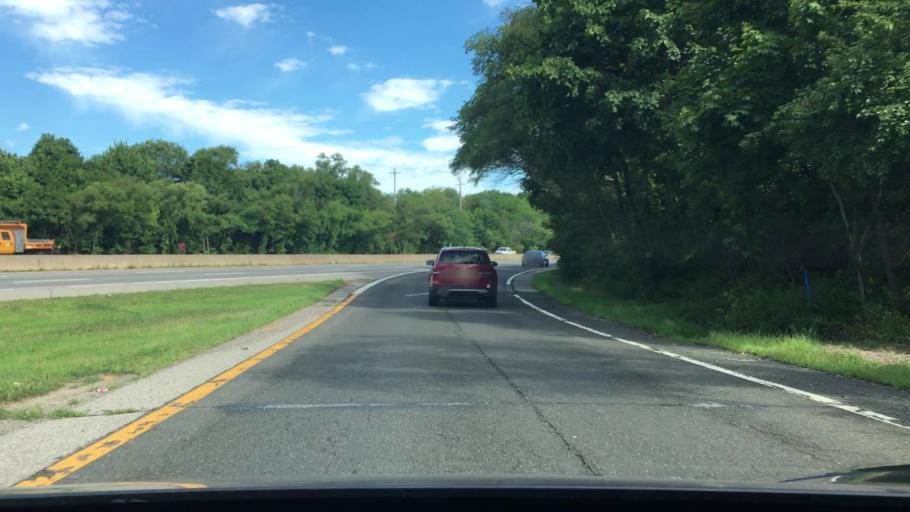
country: US
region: New York
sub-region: Nassau County
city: Plainview
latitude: 40.7752
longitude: -73.4814
